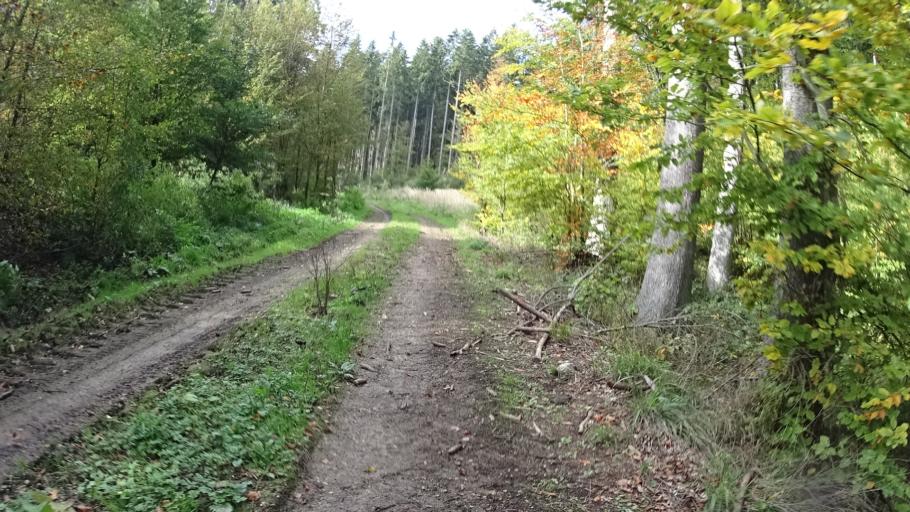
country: DE
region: Bavaria
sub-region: Upper Bavaria
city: Bohmfeld
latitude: 48.8902
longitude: 11.3411
